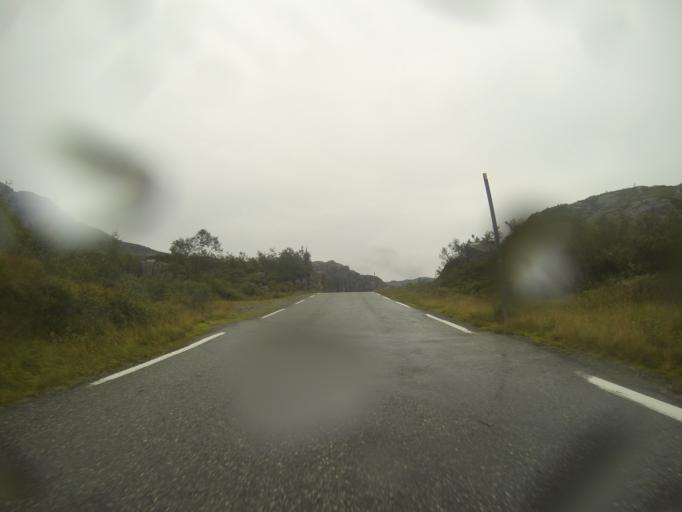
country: NO
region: Rogaland
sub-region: Sauda
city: Sauda
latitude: 59.7296
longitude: 6.5914
